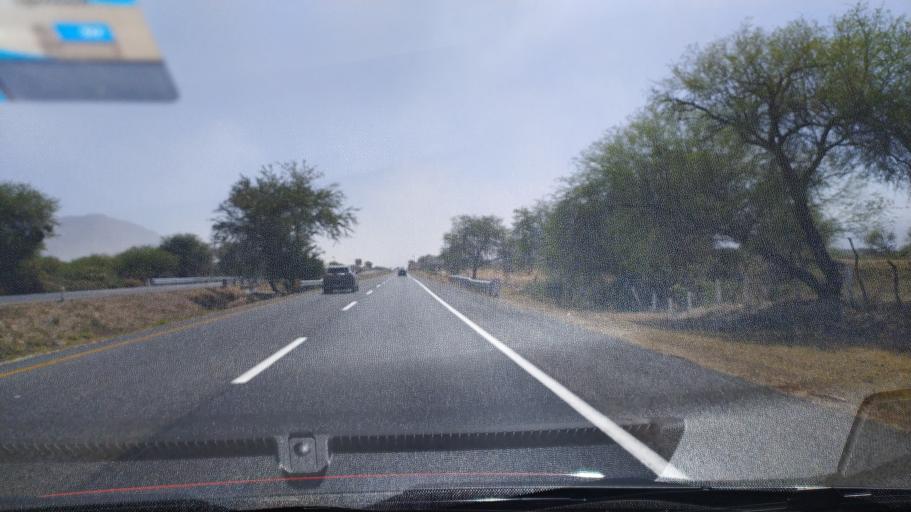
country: MX
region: Jalisco
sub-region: Acatlan de Juarez
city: Villa de los Ninos
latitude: 20.3443
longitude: -103.5734
